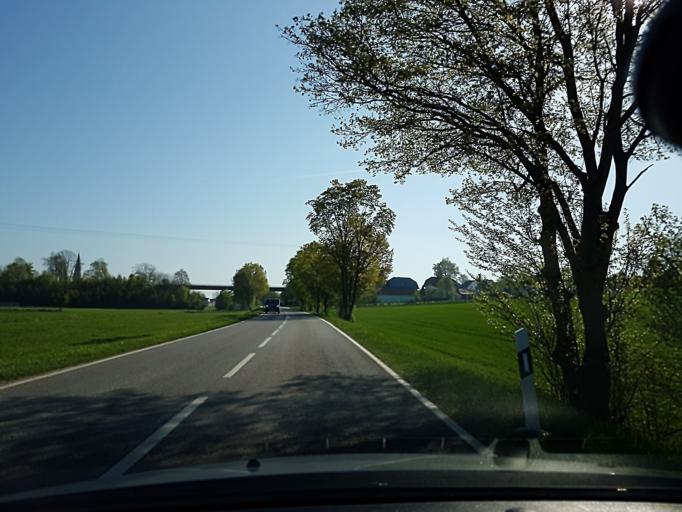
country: DE
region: Bavaria
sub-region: Lower Bavaria
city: Geisenhausen
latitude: 48.4694
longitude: 12.2503
